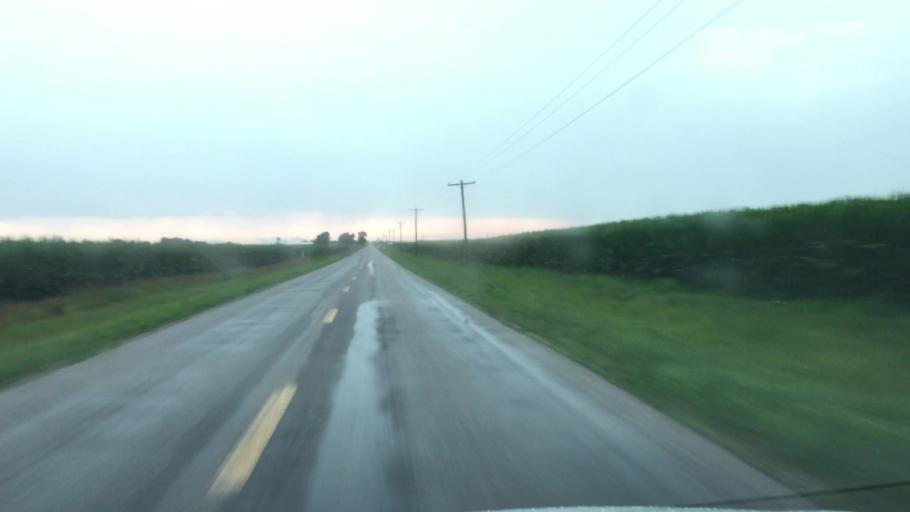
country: US
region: Iowa
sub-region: Lee County
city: Fort Madison
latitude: 40.5209
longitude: -91.2550
